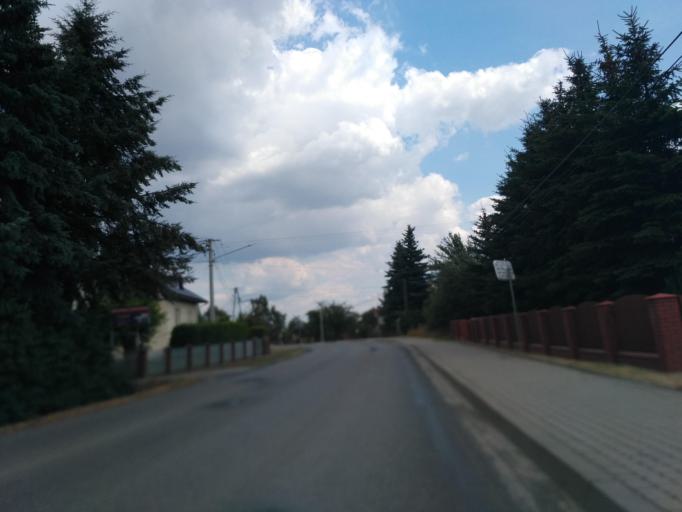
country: PL
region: Subcarpathian Voivodeship
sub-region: Powiat debicki
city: Pilzno
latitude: 50.0427
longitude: 21.3323
